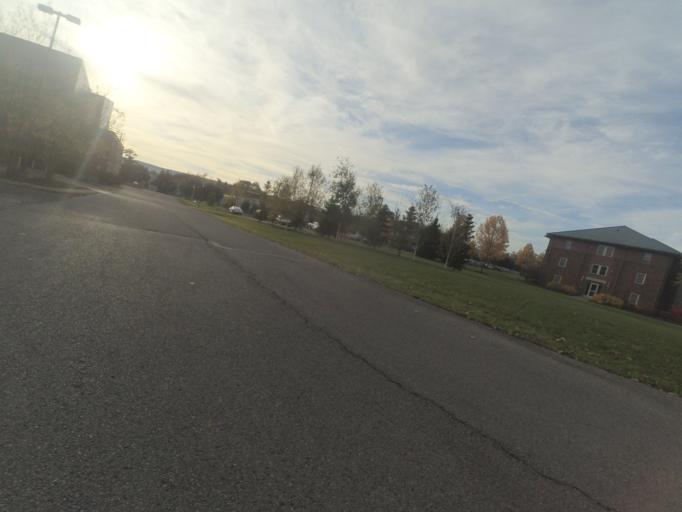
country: US
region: Pennsylvania
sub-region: Centre County
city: State College
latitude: 40.7907
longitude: -77.8713
